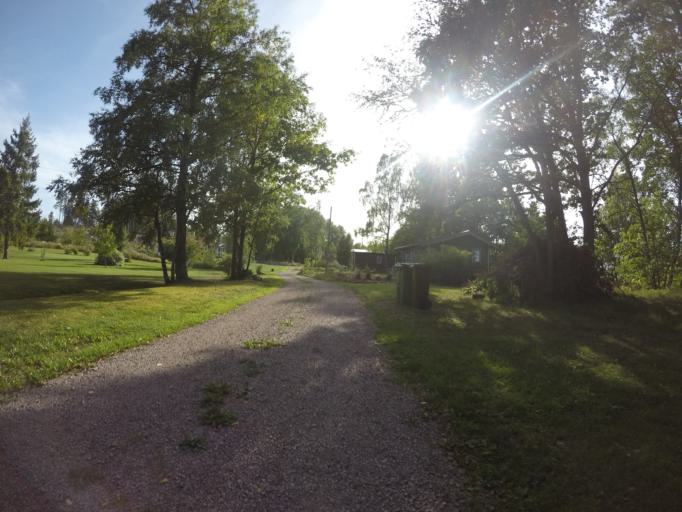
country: SE
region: Soedermanland
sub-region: Eskilstuna Kommun
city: Kvicksund
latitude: 59.5146
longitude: 16.3082
